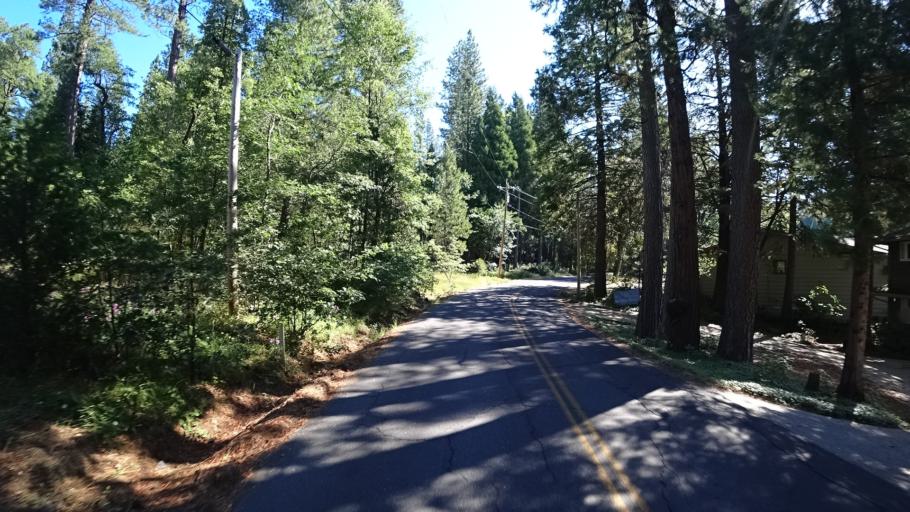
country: US
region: California
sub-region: Calaveras County
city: Arnold
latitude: 38.2521
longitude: -120.3596
